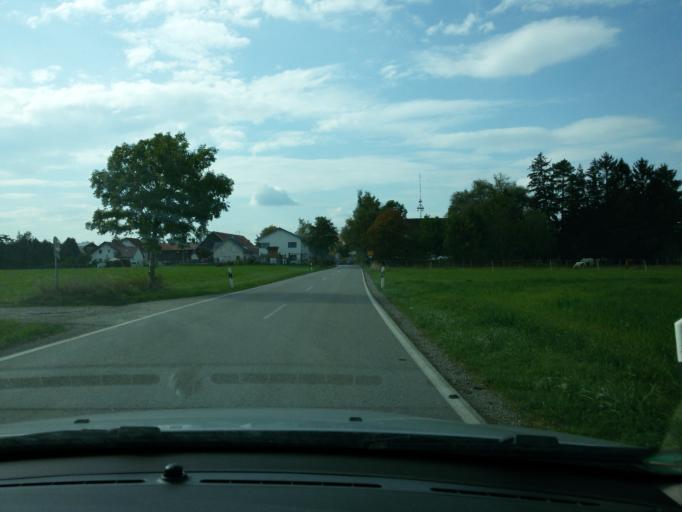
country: DE
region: Bavaria
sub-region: Swabia
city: Lamerdingen
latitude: 48.0927
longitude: 10.7439
